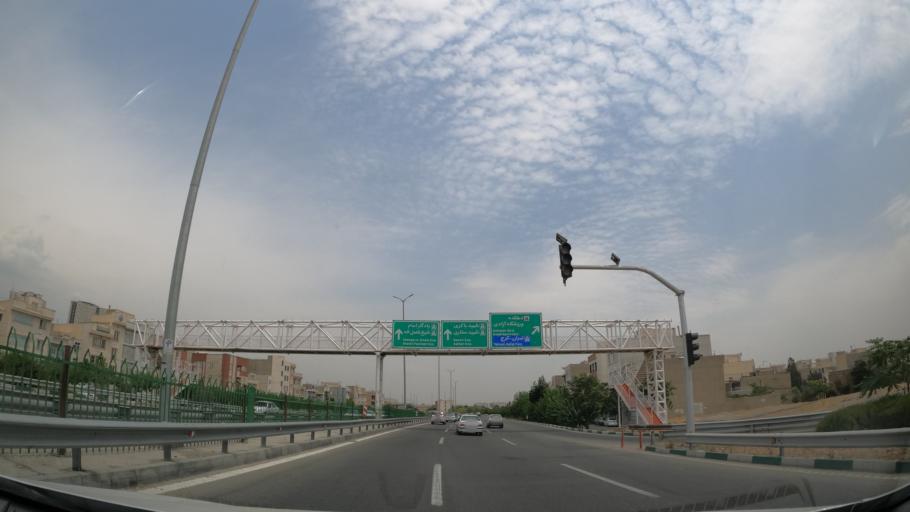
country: IR
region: Tehran
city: Shahr-e Qods
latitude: 35.7388
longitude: 51.2612
